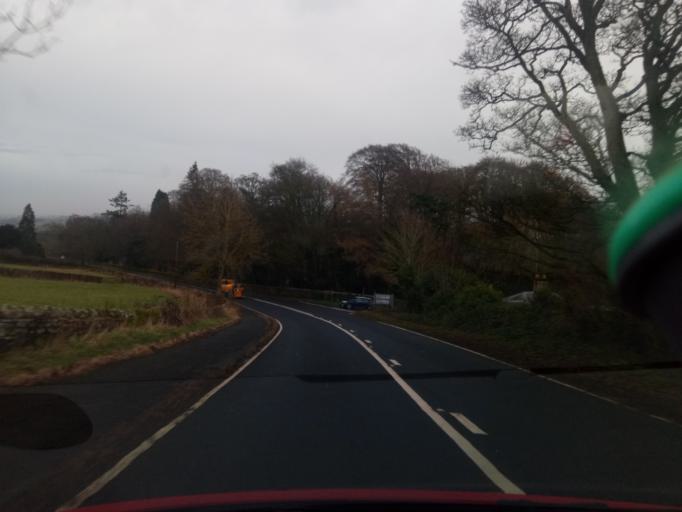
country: GB
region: England
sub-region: Northumberland
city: Wall
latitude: 55.0283
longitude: -2.1486
